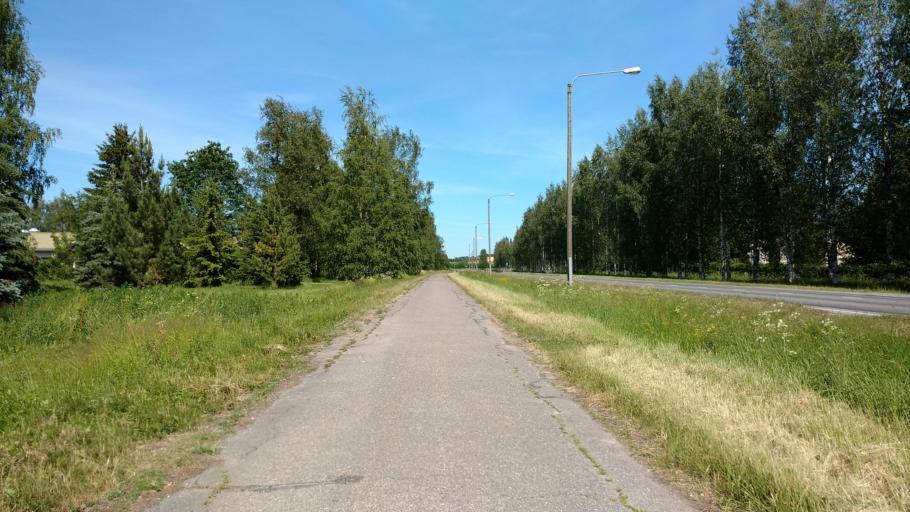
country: FI
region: Varsinais-Suomi
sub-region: Salo
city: Salo
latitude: 60.3939
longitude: 23.1495
